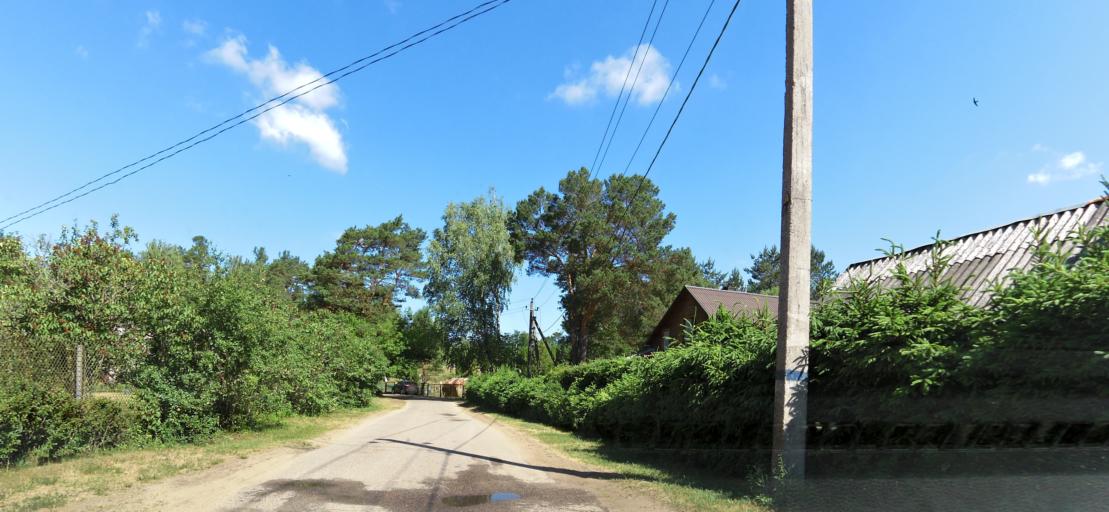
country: LT
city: Nemencine
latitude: 54.7966
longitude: 25.4021
